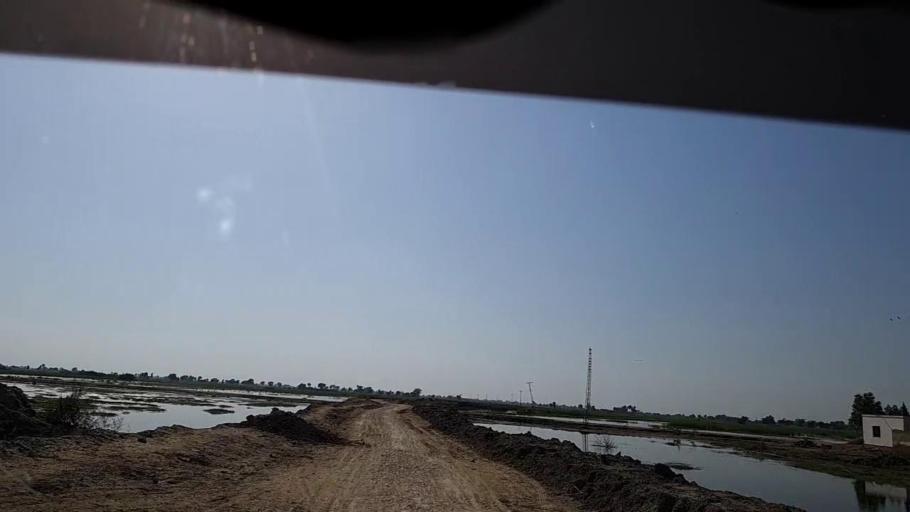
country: PK
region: Sindh
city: Tangwani
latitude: 28.3610
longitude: 69.0261
